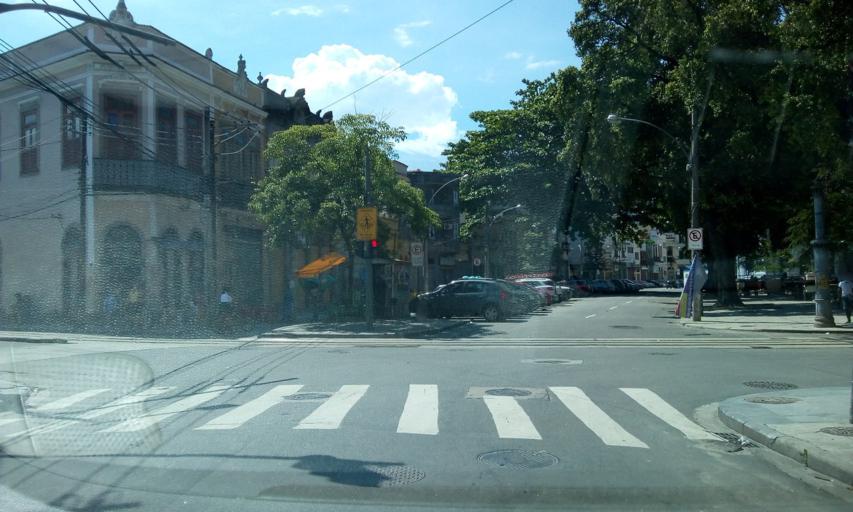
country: BR
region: Rio de Janeiro
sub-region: Rio De Janeiro
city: Rio de Janeiro
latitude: -22.8961
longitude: -43.1916
